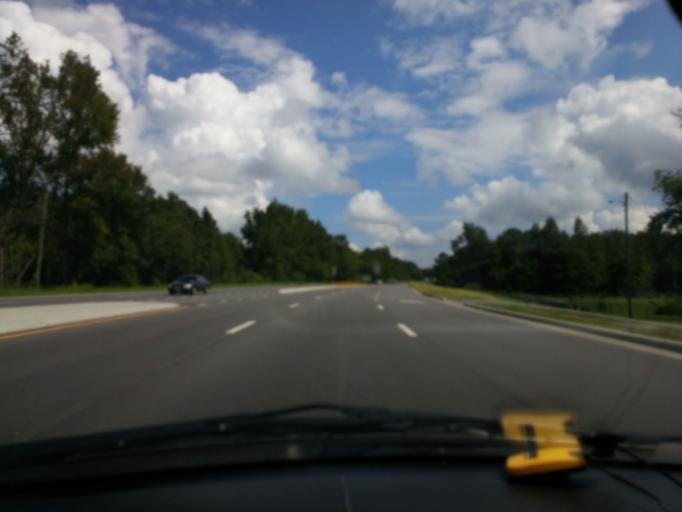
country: US
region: North Carolina
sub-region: Lenoir County
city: Kinston
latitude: 35.2555
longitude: -77.6001
